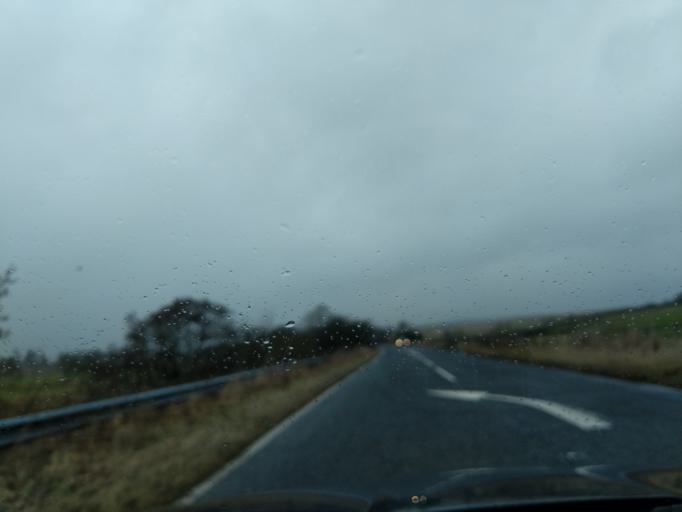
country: GB
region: England
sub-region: Northumberland
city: Otterburn
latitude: 55.2447
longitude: -2.2164
